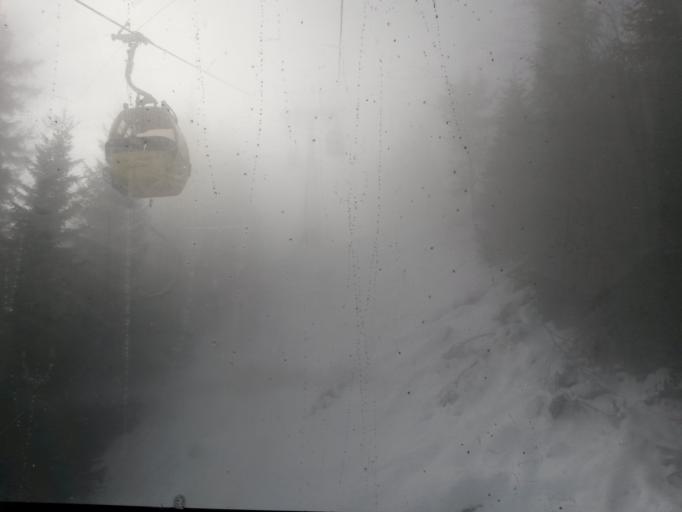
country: AT
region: Salzburg
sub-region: Politischer Bezirk Sankt Johann im Pongau
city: Dorfgastein
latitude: 47.2402
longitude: 13.1830
